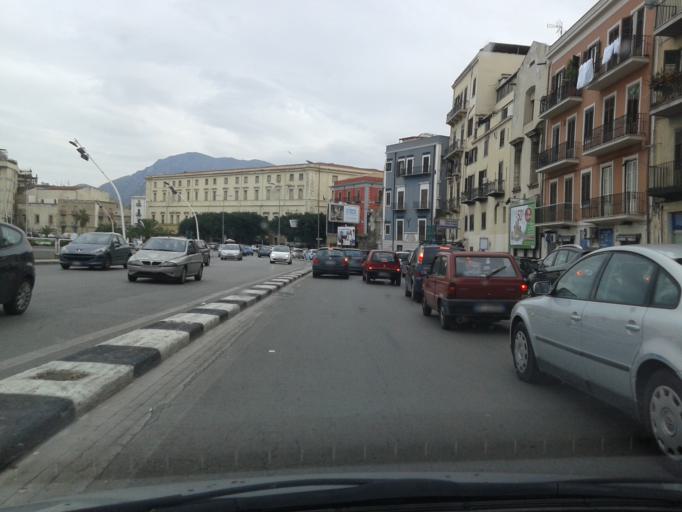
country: IT
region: Sicily
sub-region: Palermo
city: Palermo
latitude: 38.1201
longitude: 13.3665
